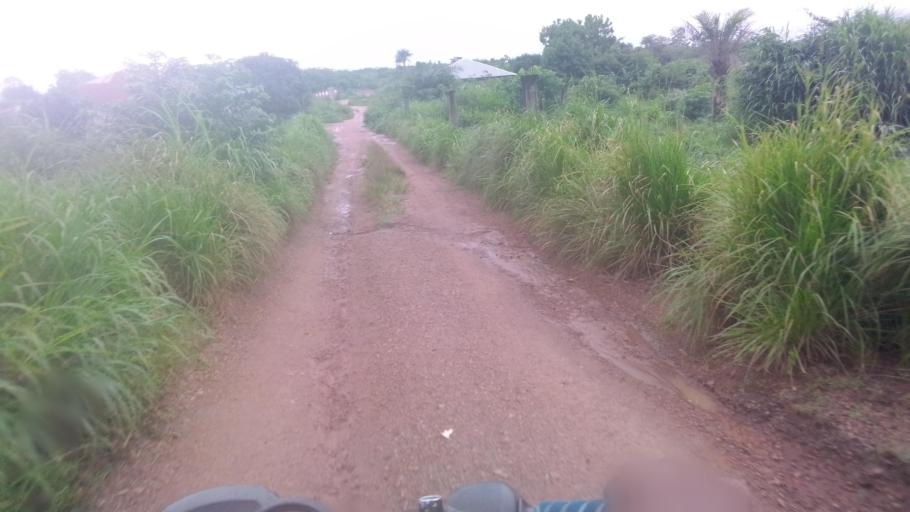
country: SL
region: Eastern Province
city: Kenema
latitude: 7.8333
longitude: -11.2119
